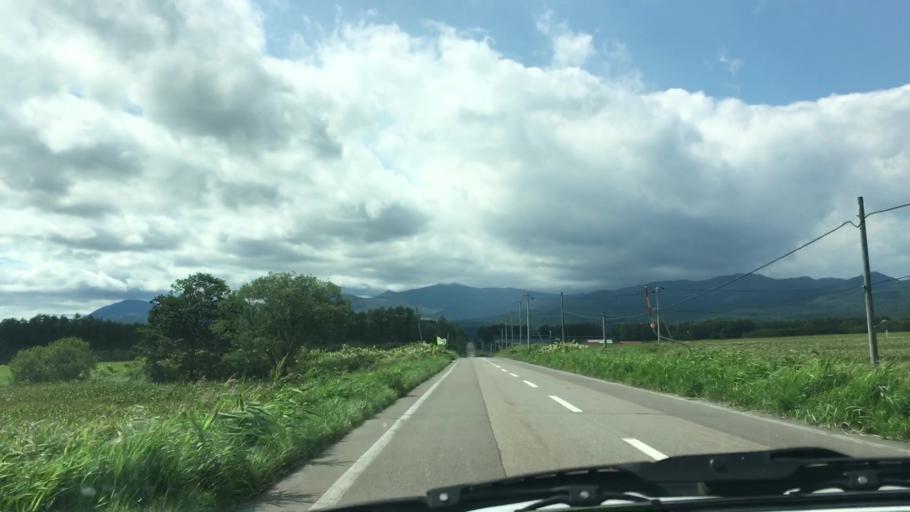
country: JP
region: Hokkaido
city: Otofuke
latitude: 43.2799
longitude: 143.3419
